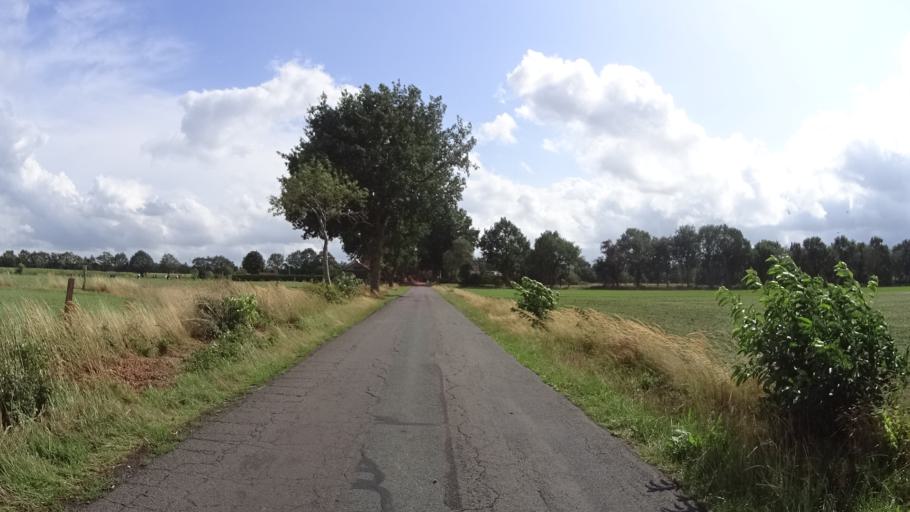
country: DE
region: Lower Saxony
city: Friedeburg
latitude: 53.3850
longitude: 7.8899
